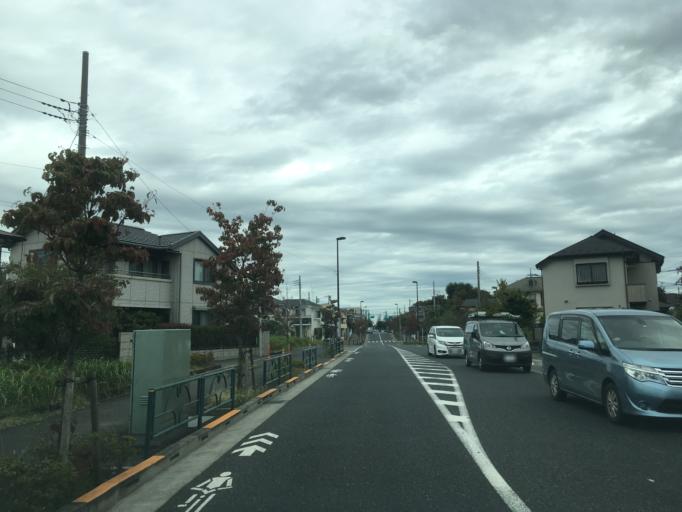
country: JP
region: Tokyo
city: Chofugaoka
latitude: 35.6304
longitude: 139.5713
